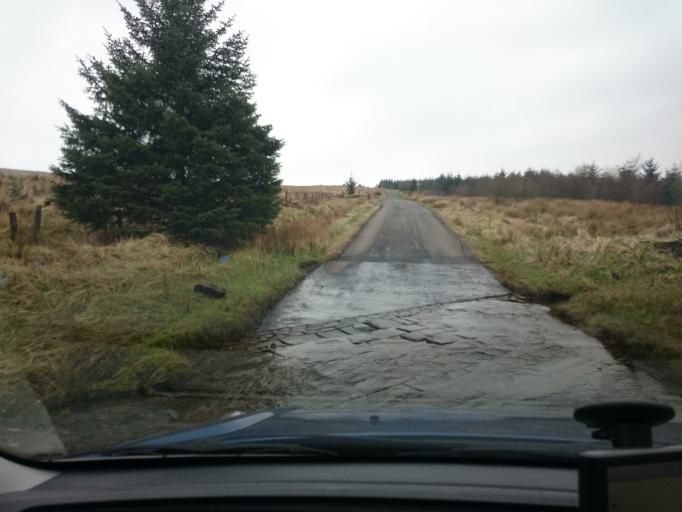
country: GB
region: Scotland
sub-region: North Lanarkshire
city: Kilsyth
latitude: 56.0163
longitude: -4.0251
